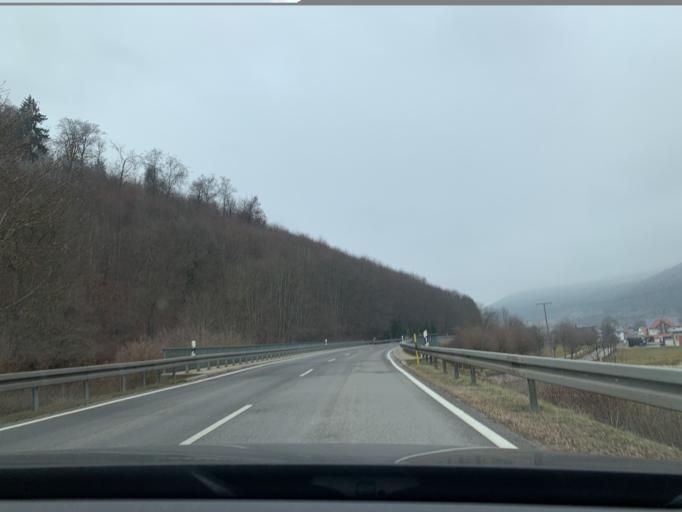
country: DE
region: Baden-Wuerttemberg
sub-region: Freiburg Region
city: Geisingen
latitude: 47.9126
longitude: 8.6747
